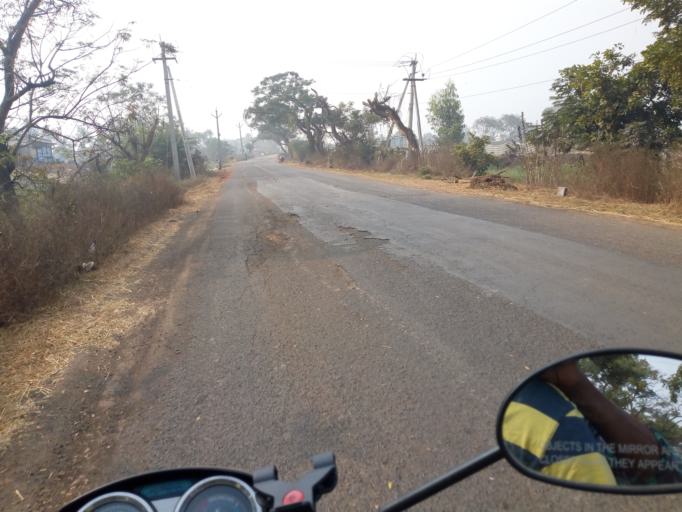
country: IN
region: Andhra Pradesh
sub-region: West Godavari
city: Tadepallegudem
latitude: 16.7475
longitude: 81.4210
